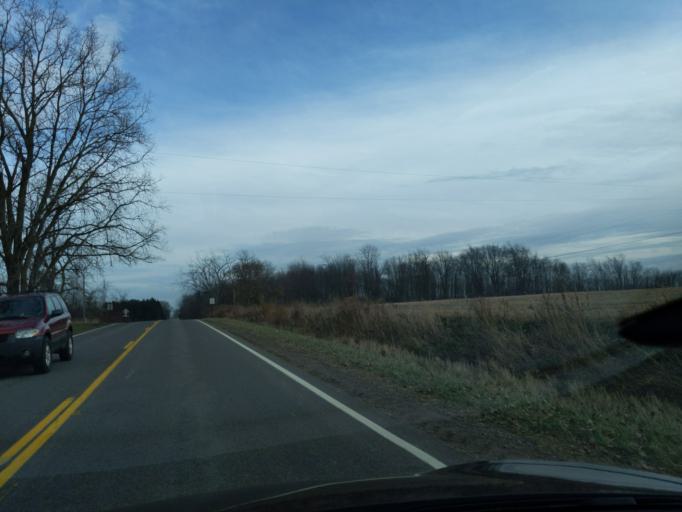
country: US
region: Michigan
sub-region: Ingham County
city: Mason
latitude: 42.6400
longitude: -84.4014
